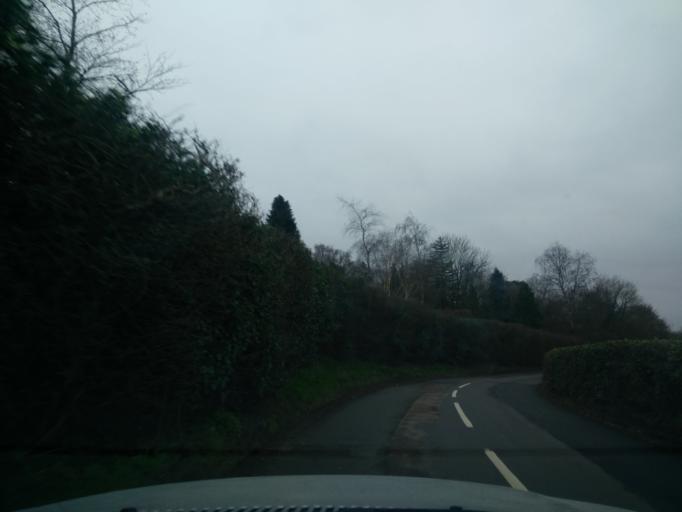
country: GB
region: England
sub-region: Buckinghamshire
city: Little Chalfont
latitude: 51.6578
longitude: -0.5734
